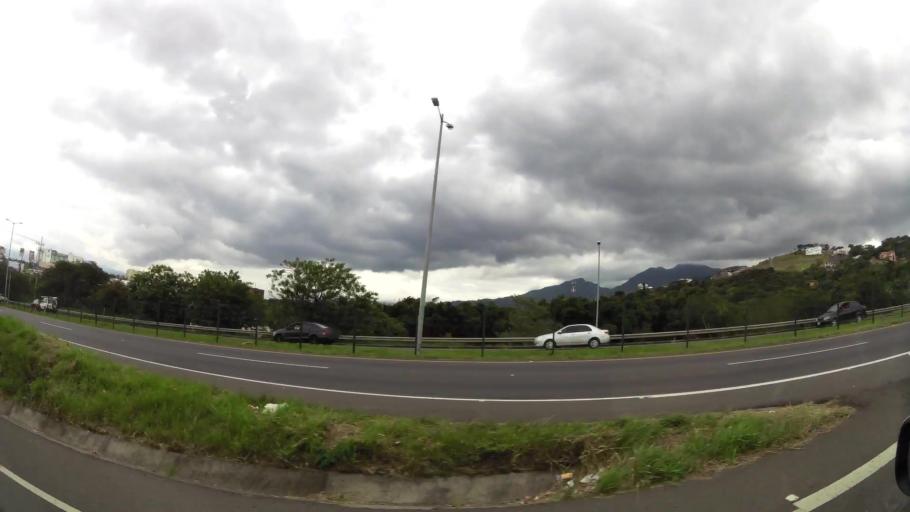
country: CR
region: San Jose
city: Santa Ana
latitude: 9.9467
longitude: -84.1629
